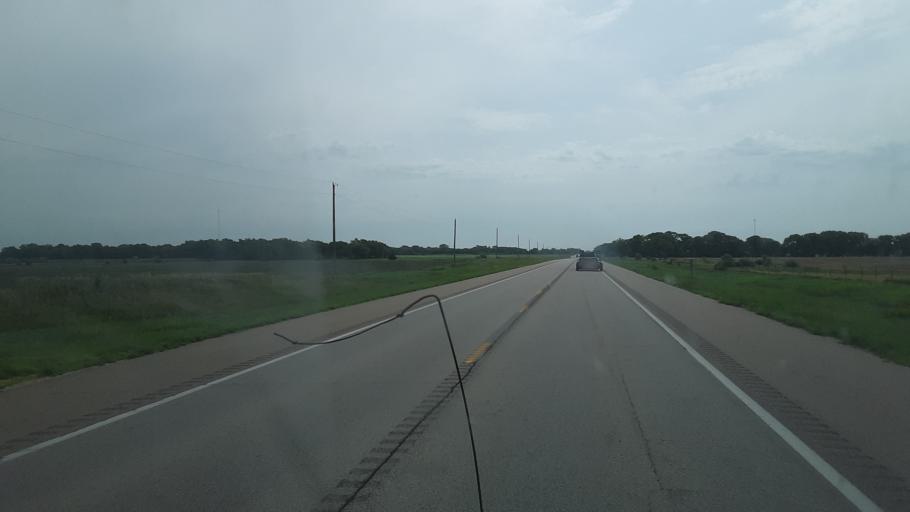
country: US
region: Kansas
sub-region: Rice County
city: Sterling
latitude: 37.9841
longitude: -98.3353
